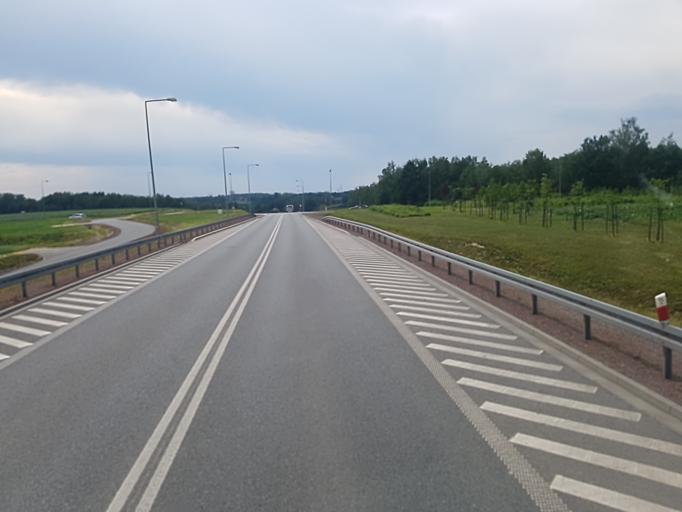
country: PL
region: Silesian Voivodeship
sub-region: Jastrzebie-Zdroj
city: Jastrzebie Zdroj
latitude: 49.9711
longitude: 18.6072
